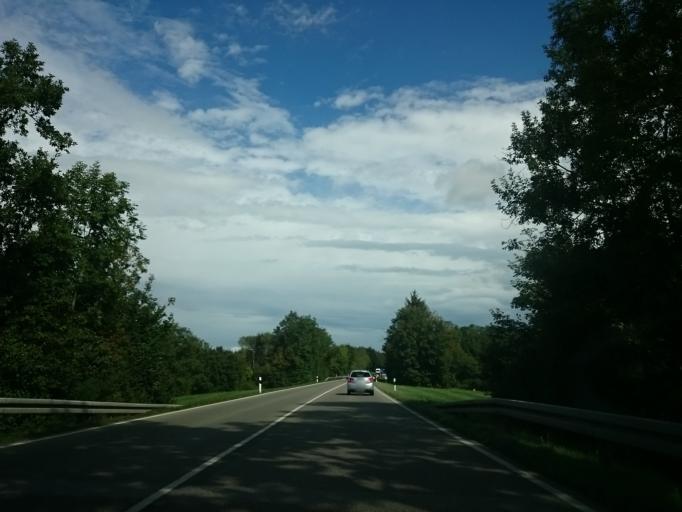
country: DE
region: Bavaria
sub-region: Swabia
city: Mauerstetten
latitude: 47.8962
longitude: 10.6481
